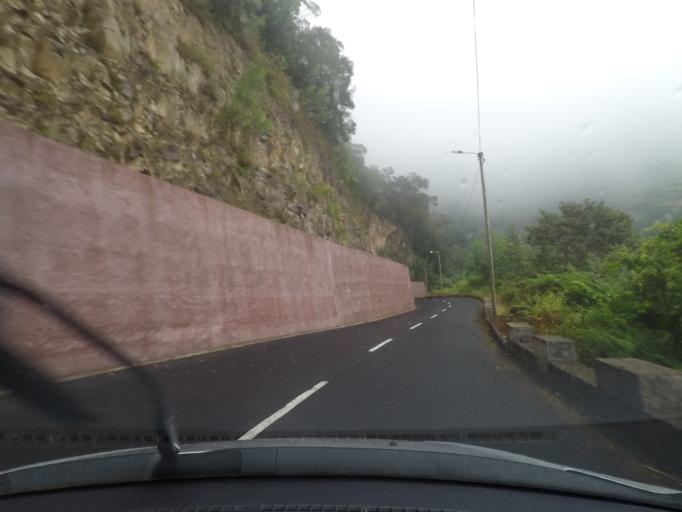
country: PT
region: Madeira
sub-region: Santana
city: Santana
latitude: 32.7752
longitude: -16.8742
